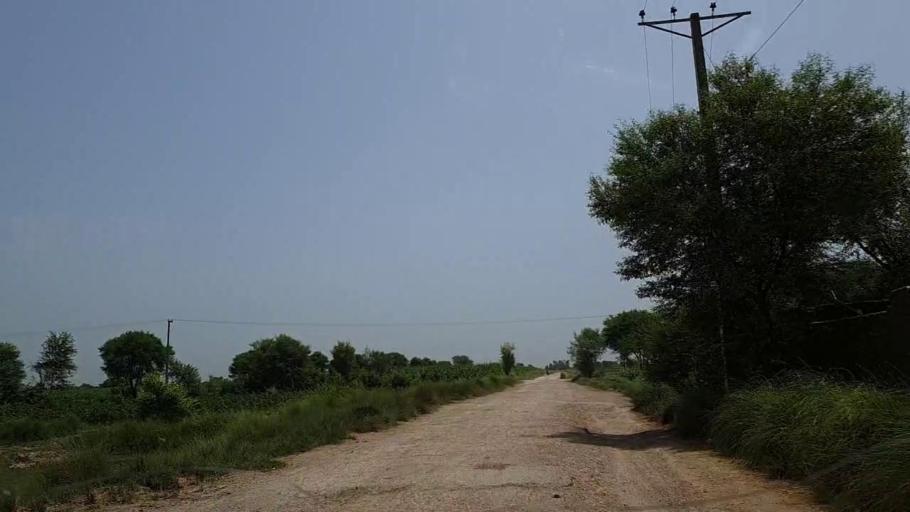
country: PK
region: Sindh
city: Naushahro Firoz
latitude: 26.8429
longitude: 67.9881
